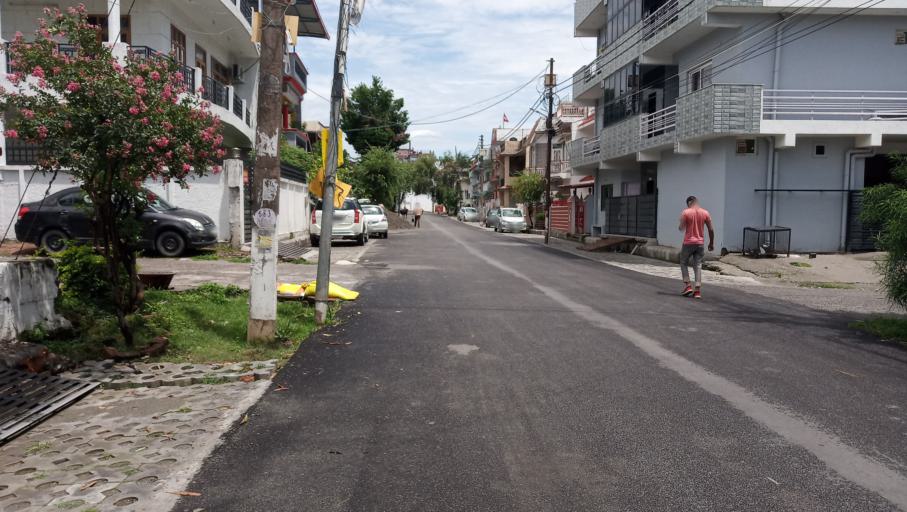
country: IN
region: Uttarakhand
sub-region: Dehradun
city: Dehradun
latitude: 30.3653
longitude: 78.0657
